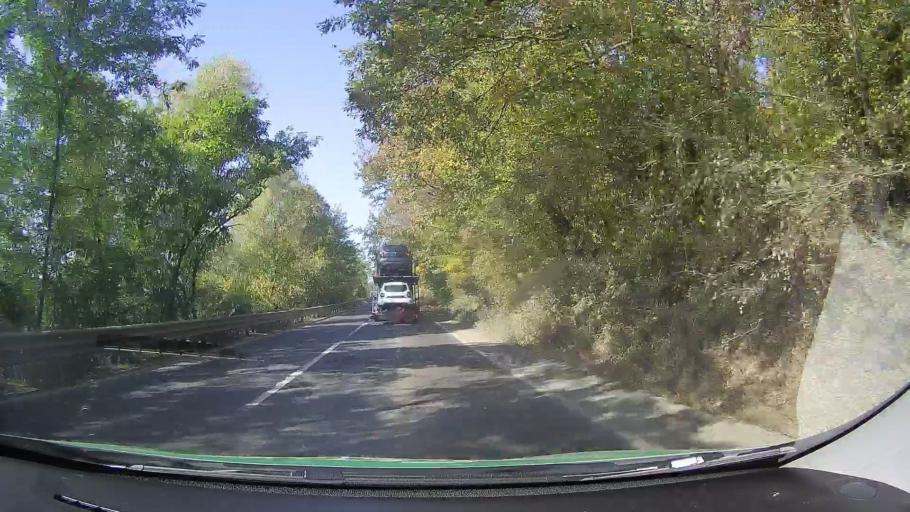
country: RO
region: Arad
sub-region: Comuna Bata
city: Bata
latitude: 46.0734
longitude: 22.0359
